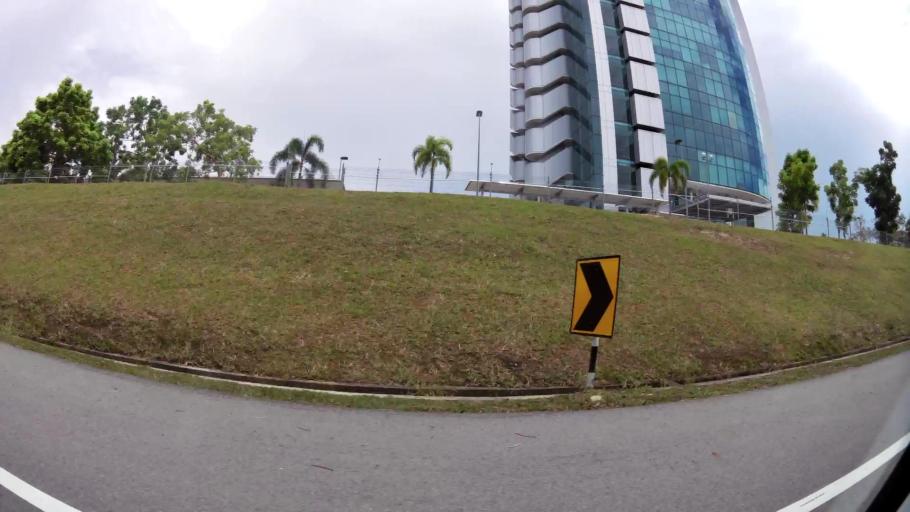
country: BN
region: Brunei and Muara
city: Bandar Seri Begawan
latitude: 4.9662
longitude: 114.8853
